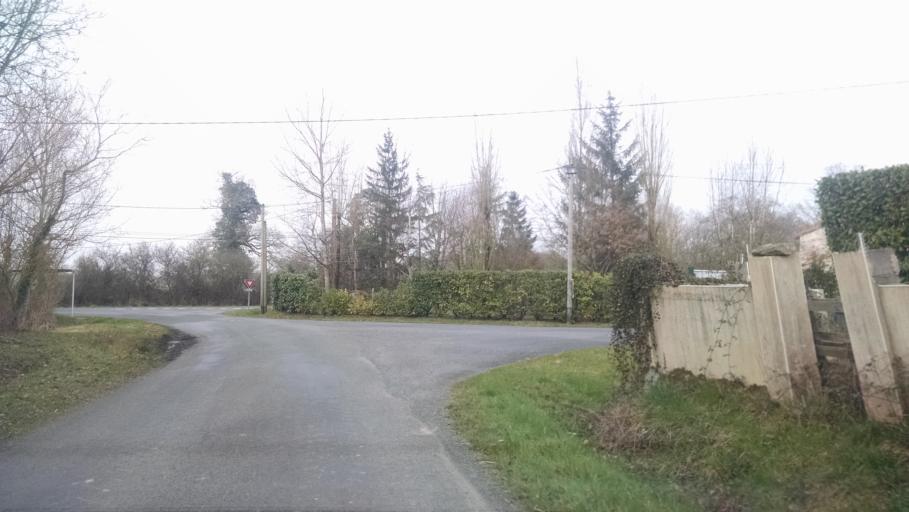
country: FR
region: Pays de la Loire
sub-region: Departement de la Loire-Atlantique
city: Saint-Lumine-de-Clisson
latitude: 47.0680
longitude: -1.3513
